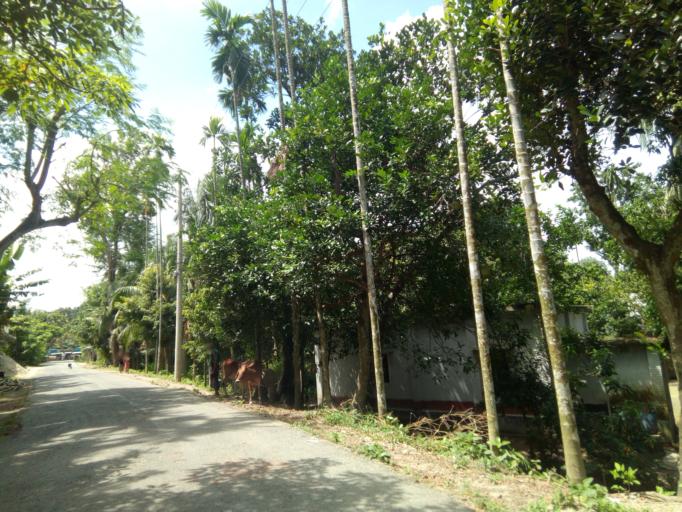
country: BD
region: Khulna
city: Kalia
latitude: 23.0172
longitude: 89.7175
